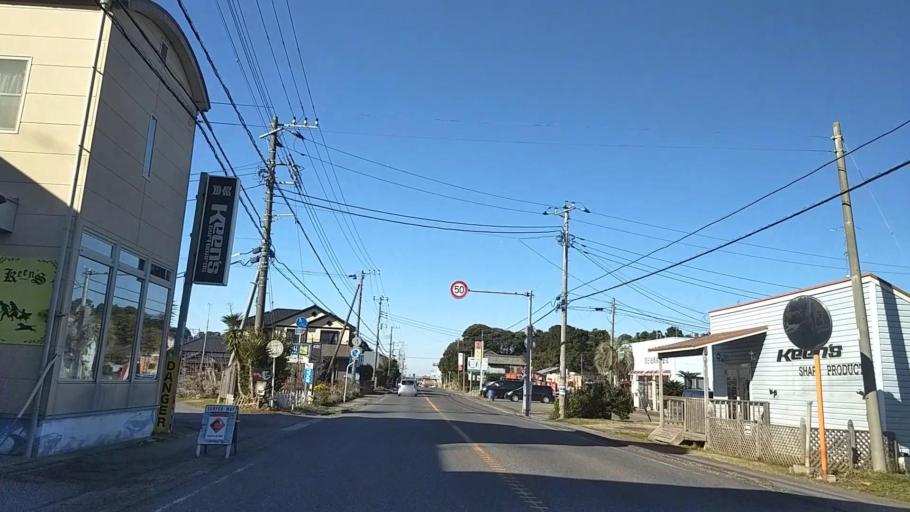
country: JP
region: Chiba
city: Ohara
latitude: 35.3277
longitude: 140.3980
